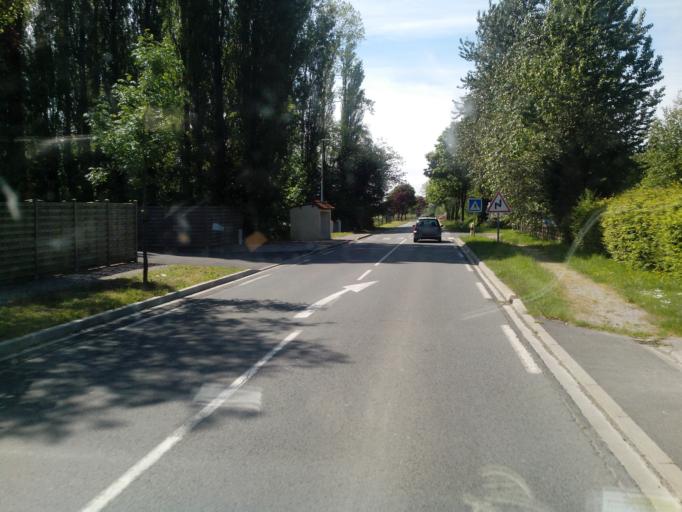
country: FR
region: Nord-Pas-de-Calais
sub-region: Departement du Pas-de-Calais
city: Montreuil
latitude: 50.4937
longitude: 1.7147
